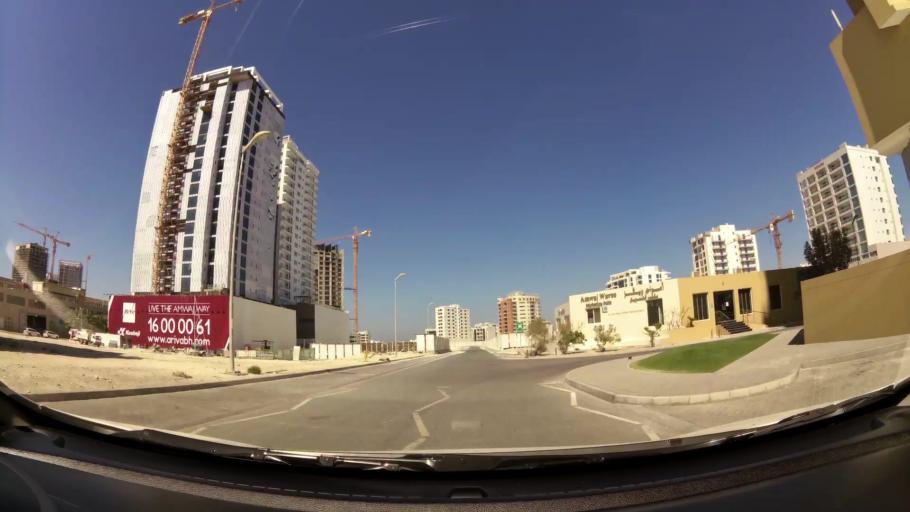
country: BH
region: Muharraq
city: Al Hadd
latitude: 26.2872
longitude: 50.6657
